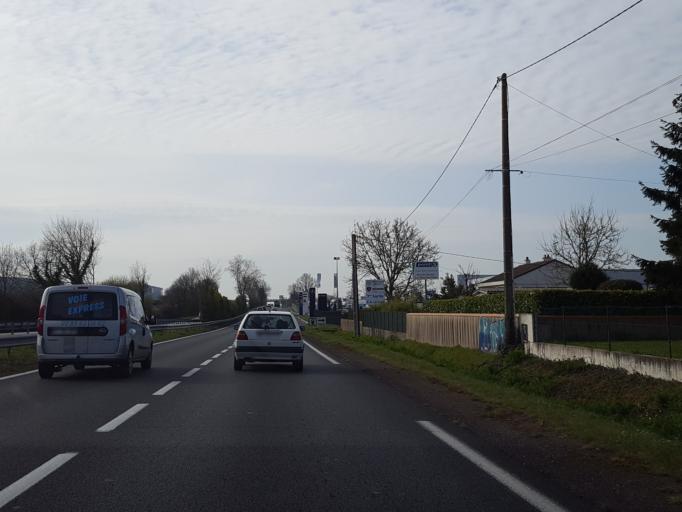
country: FR
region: Pays de la Loire
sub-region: Departement de la Vendee
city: Belleville-sur-Vie
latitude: 46.7514
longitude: -1.4306
